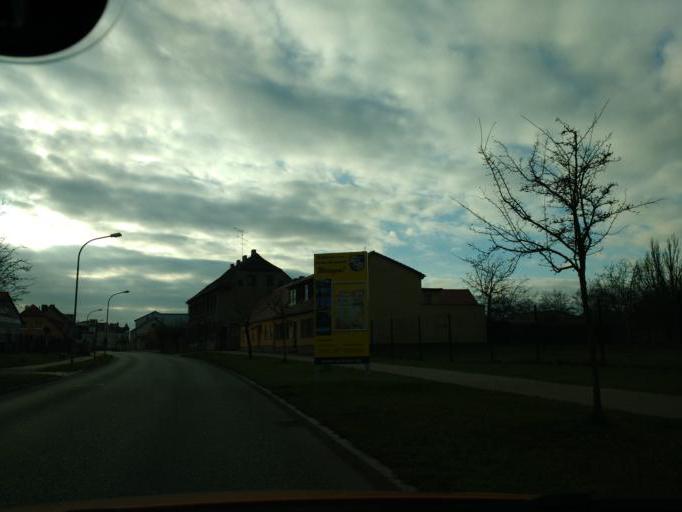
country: DE
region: Brandenburg
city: Wriezen
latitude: 52.7226
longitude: 14.1392
